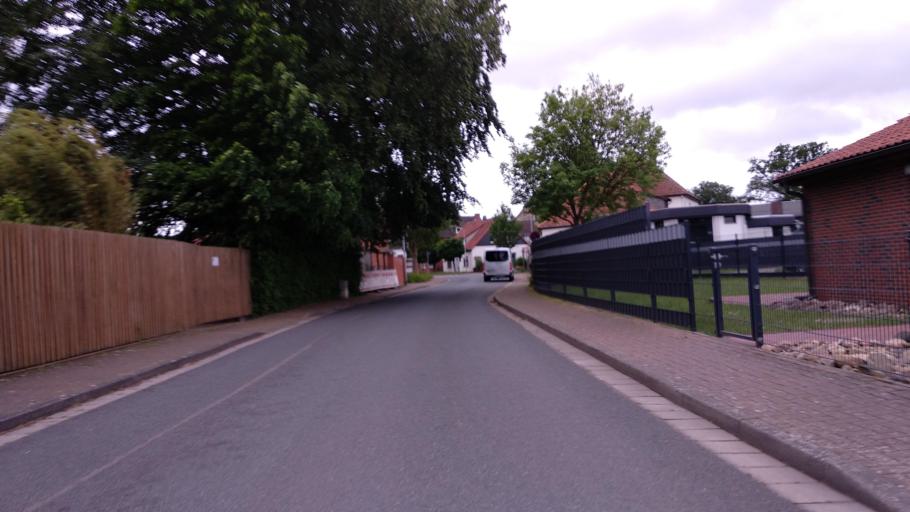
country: DE
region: Lower Saxony
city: Hagenburg
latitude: 52.4570
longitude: 9.3580
